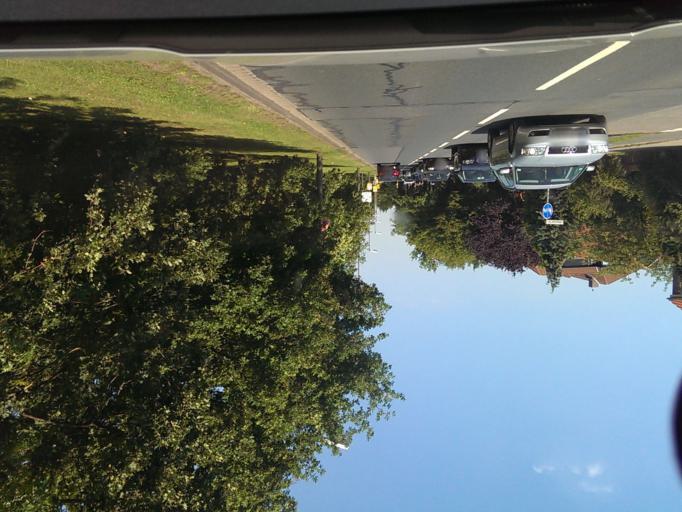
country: DE
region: Lower Saxony
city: Langenhagen
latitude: 52.4379
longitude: 9.7548
